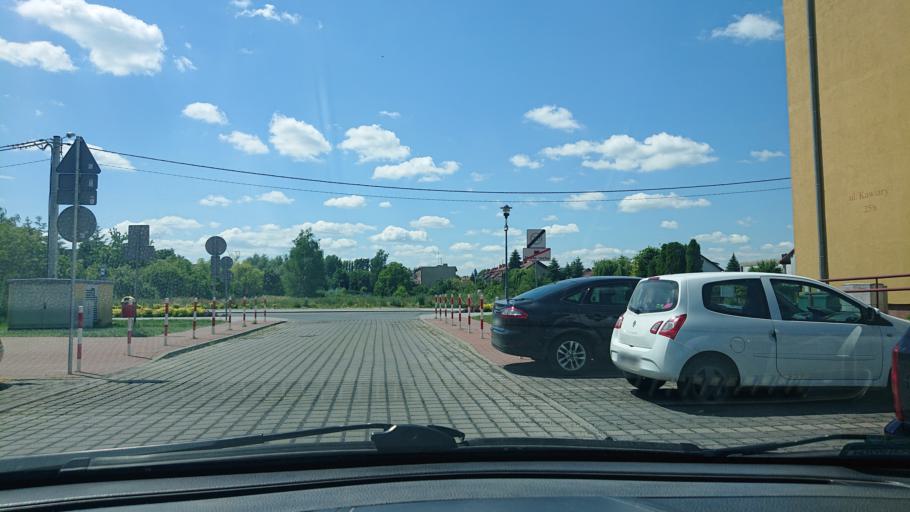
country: PL
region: Greater Poland Voivodeship
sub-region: Powiat gnieznienski
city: Gniezno
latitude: 52.5213
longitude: 17.6136
